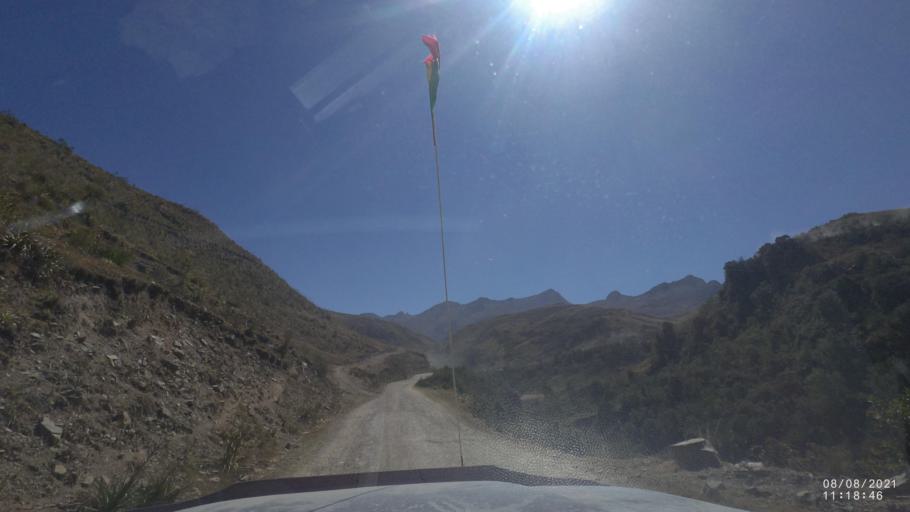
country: BO
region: Cochabamba
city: Colchani
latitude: -16.7802
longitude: -66.6625
